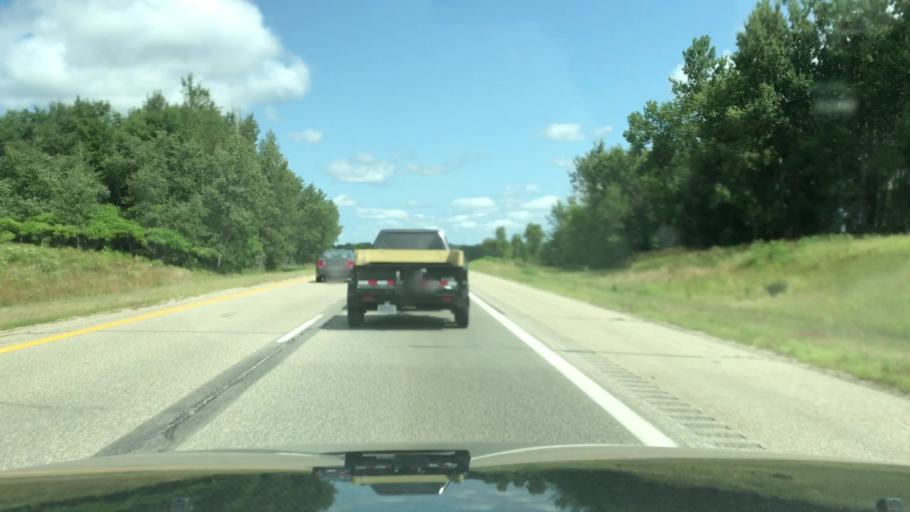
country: US
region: Michigan
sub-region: Mecosta County
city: Big Rapids
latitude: 43.7247
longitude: -85.5320
